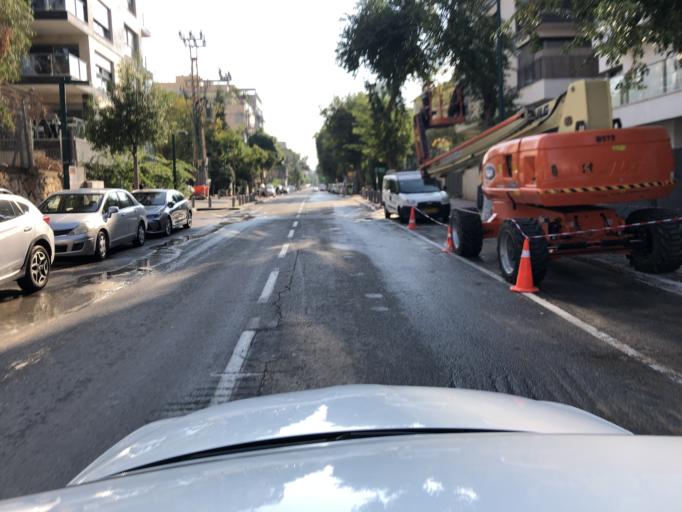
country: IL
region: Tel Aviv
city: Ramat Gan
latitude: 32.0858
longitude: 34.8198
